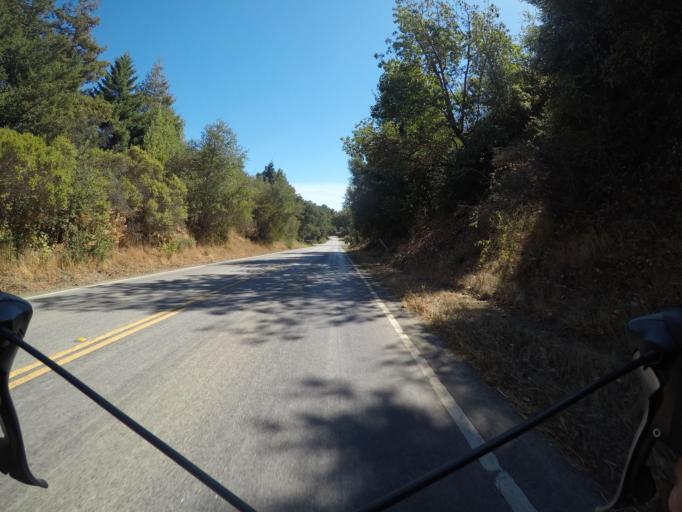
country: US
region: California
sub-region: San Mateo County
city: Portola Valley
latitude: 37.3419
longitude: -122.2222
